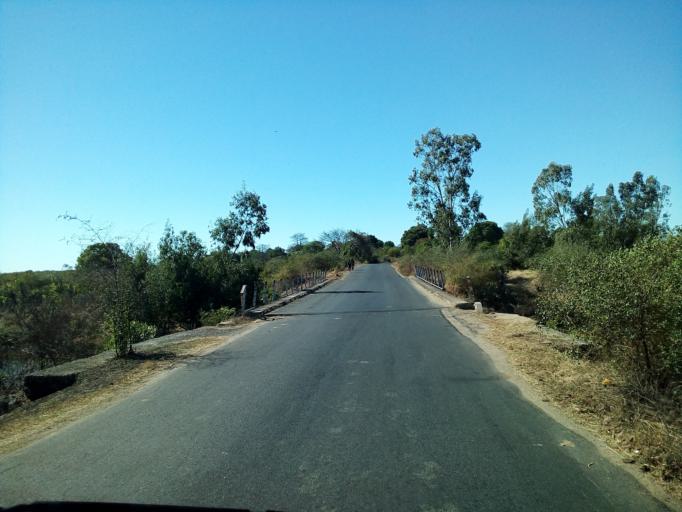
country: MG
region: Boeny
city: Marovoay
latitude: -16.0035
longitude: 46.6945
